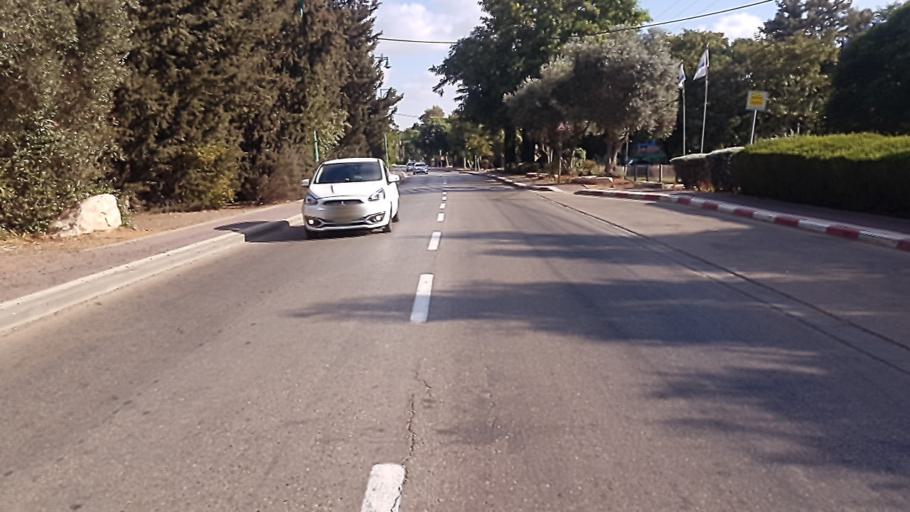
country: IL
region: Central District
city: Jaljulya
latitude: 32.1738
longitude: 34.9392
